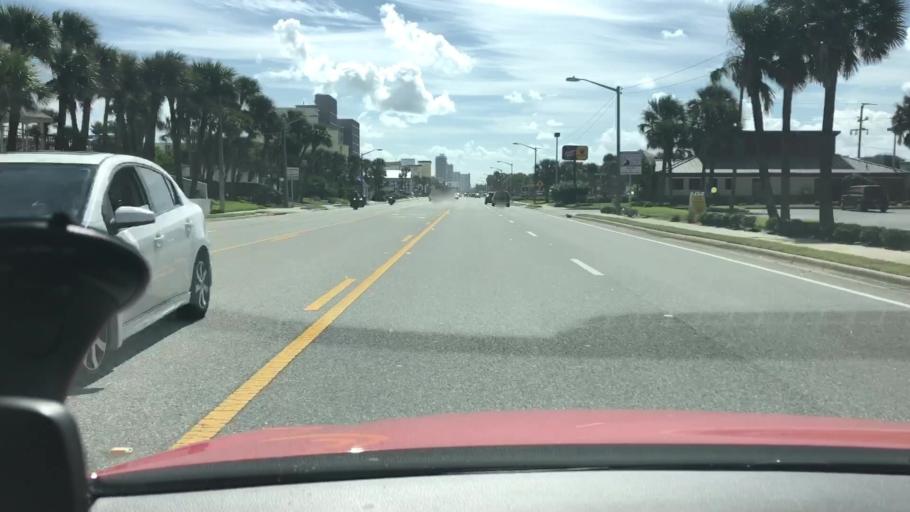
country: US
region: Florida
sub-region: Volusia County
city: Ormond Beach
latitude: 29.2816
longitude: -81.0349
